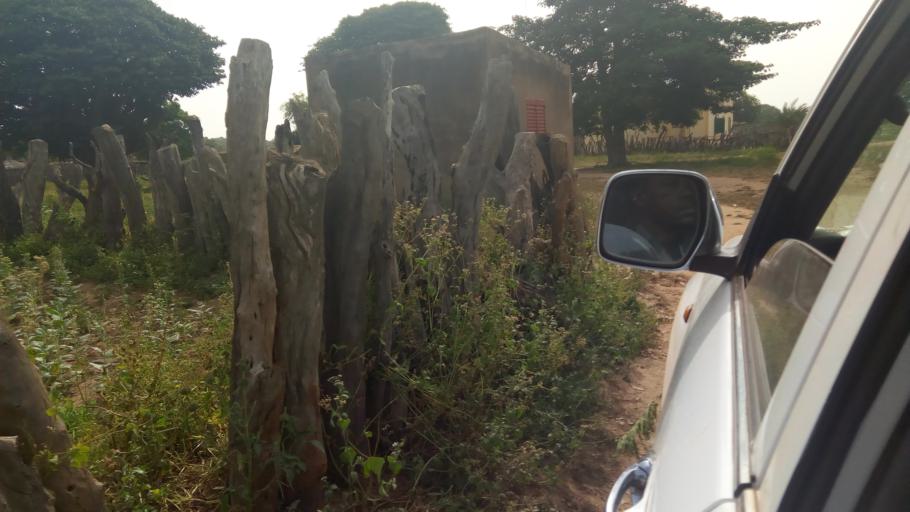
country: ML
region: Kayes
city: Kita
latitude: 13.1421
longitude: -8.8657
